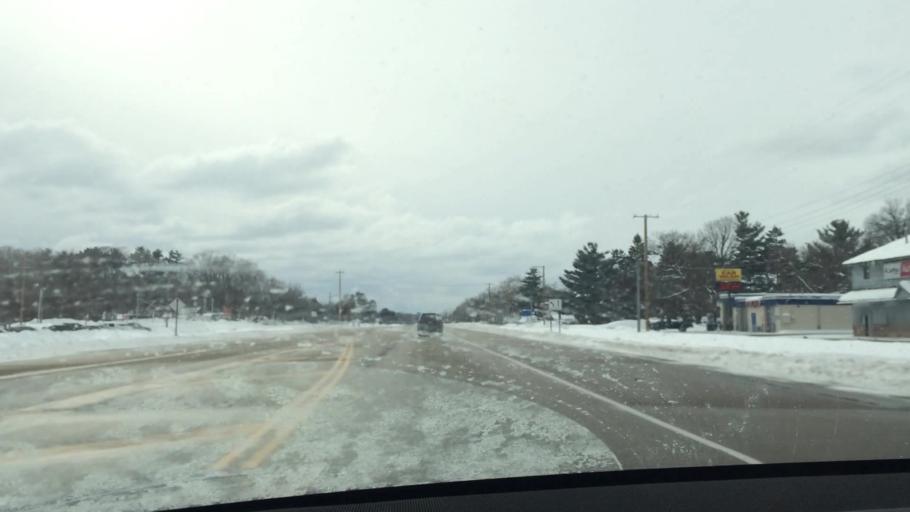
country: US
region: Minnesota
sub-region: Anoka County
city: Lexington
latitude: 45.1371
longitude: -93.1717
